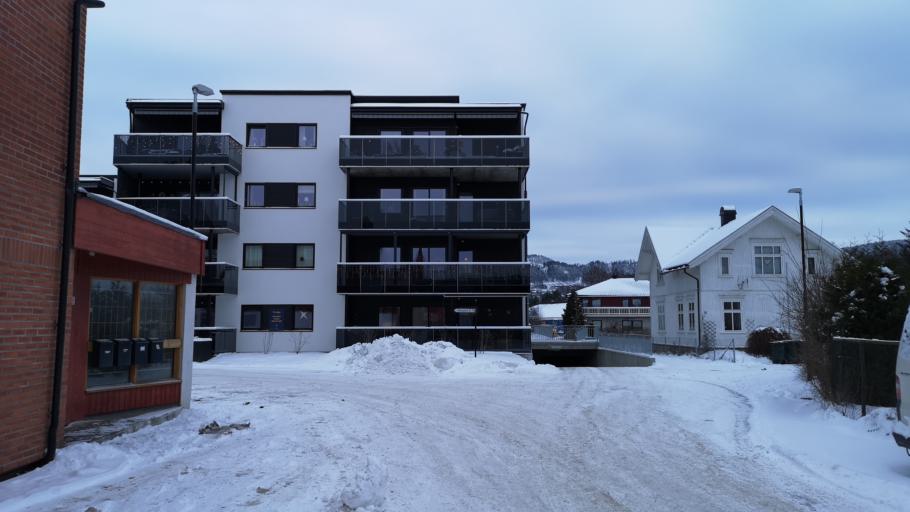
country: NO
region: Buskerud
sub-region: Ovre Eiker
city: Hokksund
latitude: 59.7686
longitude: 9.9119
